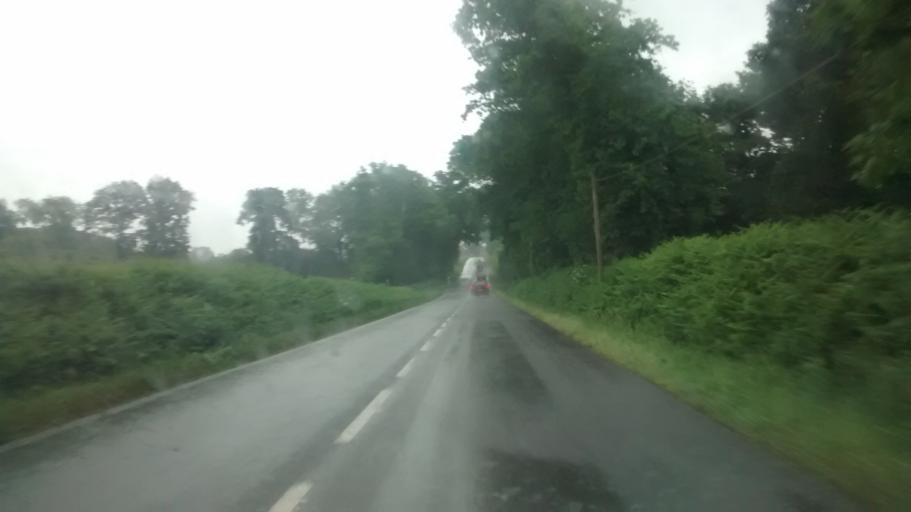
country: FR
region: Brittany
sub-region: Departement du Morbihan
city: La Gacilly
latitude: 47.7791
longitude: -2.1647
